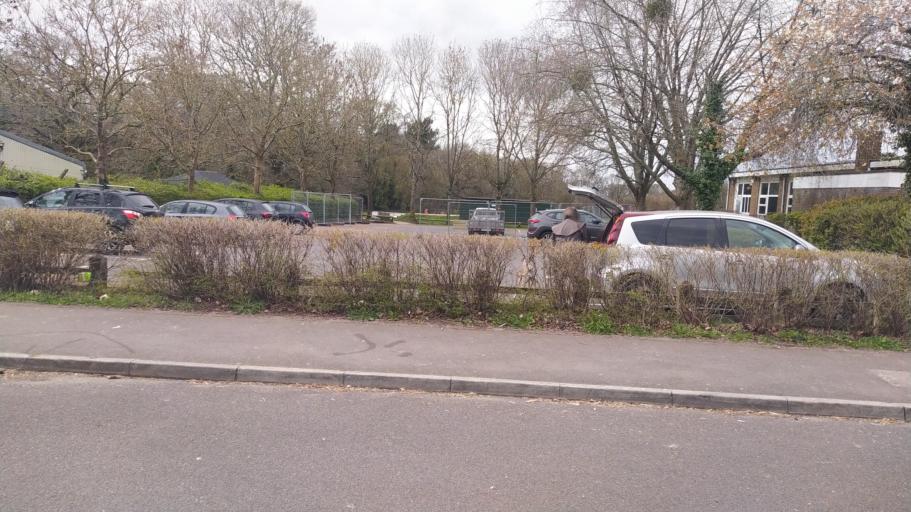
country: GB
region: England
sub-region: Hampshire
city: Totton
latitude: 50.9442
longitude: -1.4630
